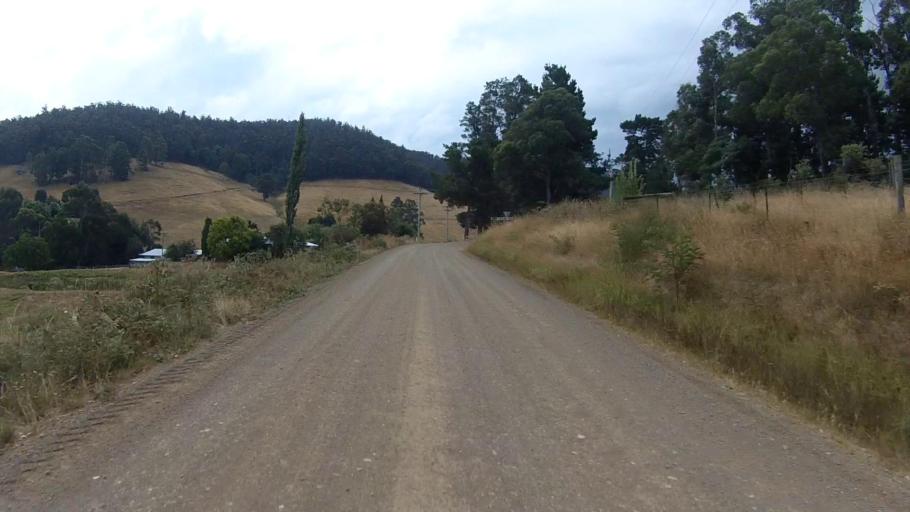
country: AU
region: Tasmania
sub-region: Huon Valley
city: Huonville
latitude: -42.9722
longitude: 147.0541
